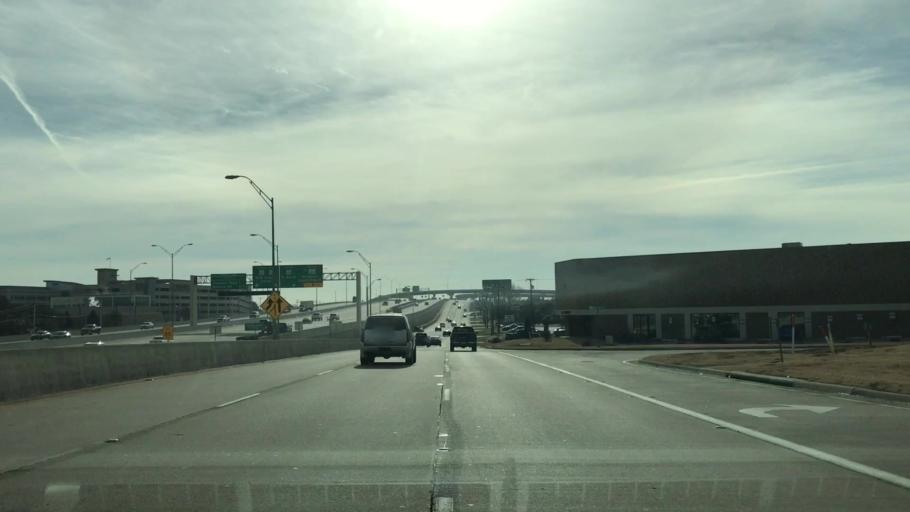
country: US
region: Texas
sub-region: Tarrant County
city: Grapevine
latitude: 32.9363
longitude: -97.0988
